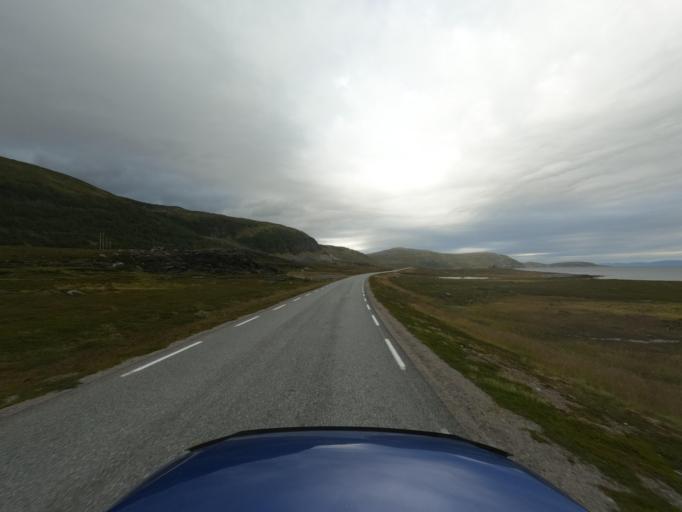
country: NO
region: Finnmark Fylke
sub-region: Nordkapp
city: Honningsvag
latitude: 70.7598
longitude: 25.5948
